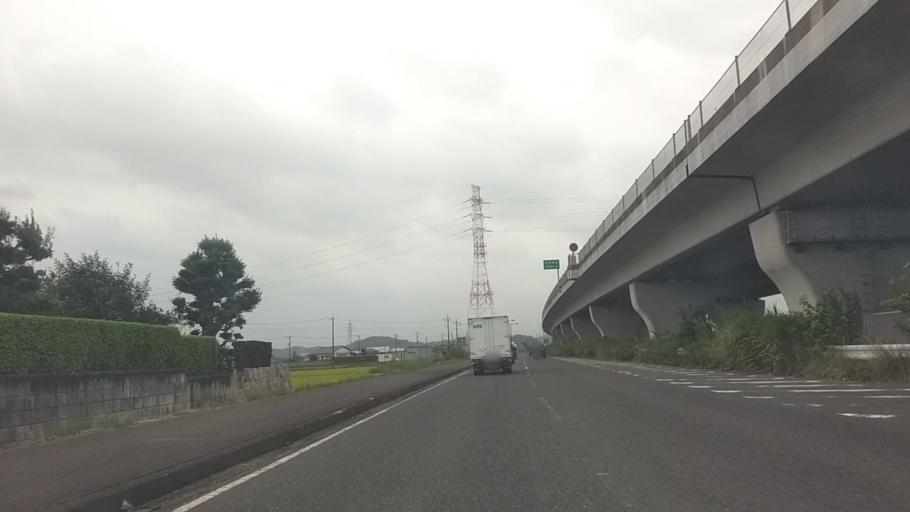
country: JP
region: Chiba
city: Kisarazu
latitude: 35.4024
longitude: 139.9665
